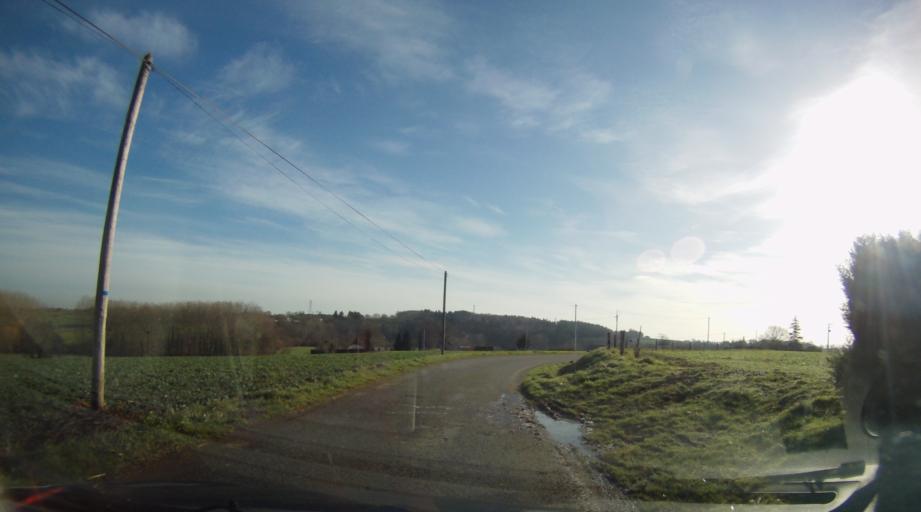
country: FR
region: Brittany
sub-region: Departement d'Ille-et-Vilaine
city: Bourgbarre
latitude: 47.9884
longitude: -1.6055
